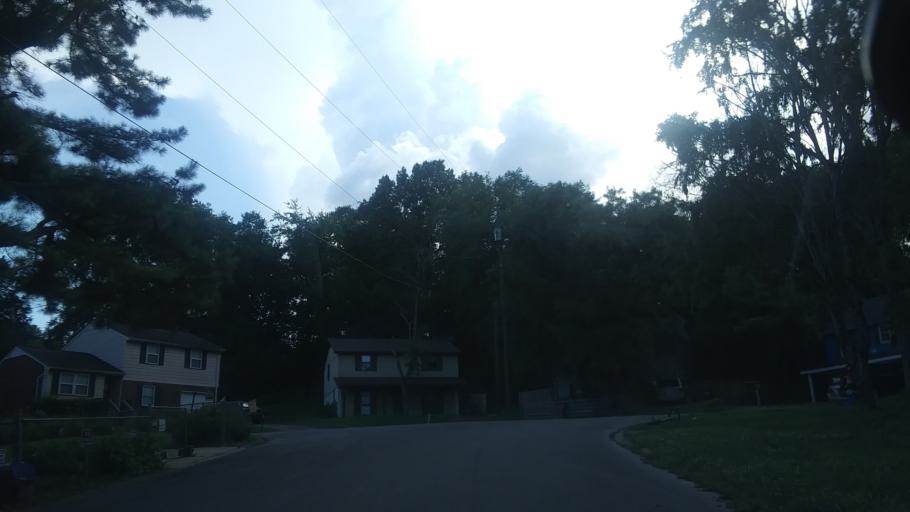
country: US
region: Tennessee
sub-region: Rutherford County
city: La Vergne
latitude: 36.0706
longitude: -86.6655
